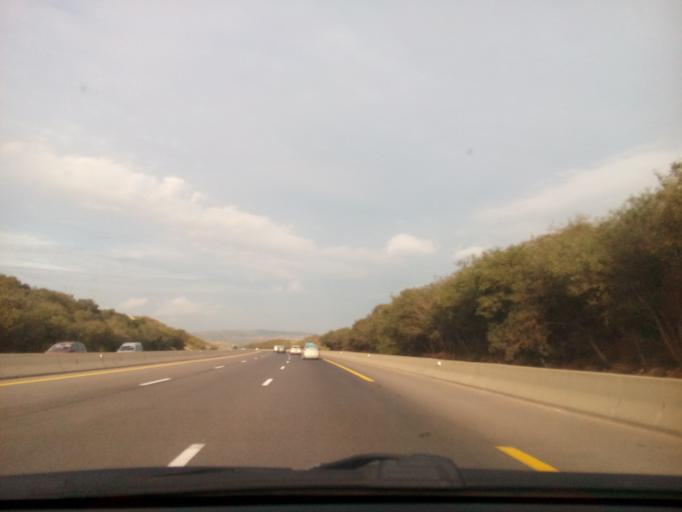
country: DZ
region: Relizane
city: Relizane
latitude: 35.7599
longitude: 0.3657
